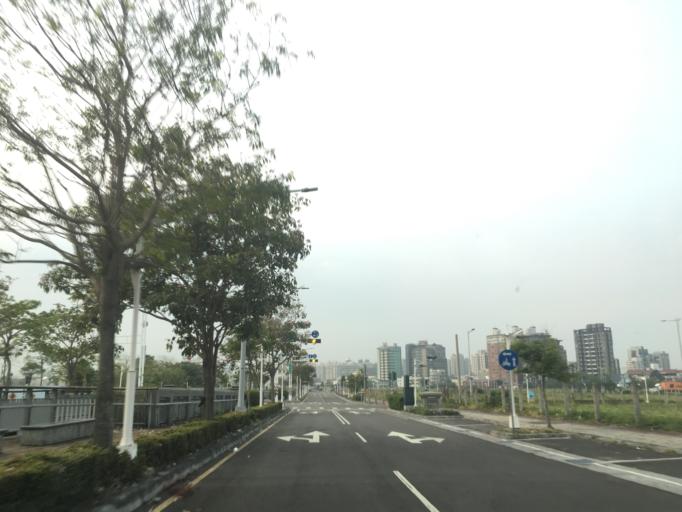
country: TW
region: Taiwan
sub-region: Taichung City
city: Taichung
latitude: 24.1974
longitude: 120.6683
